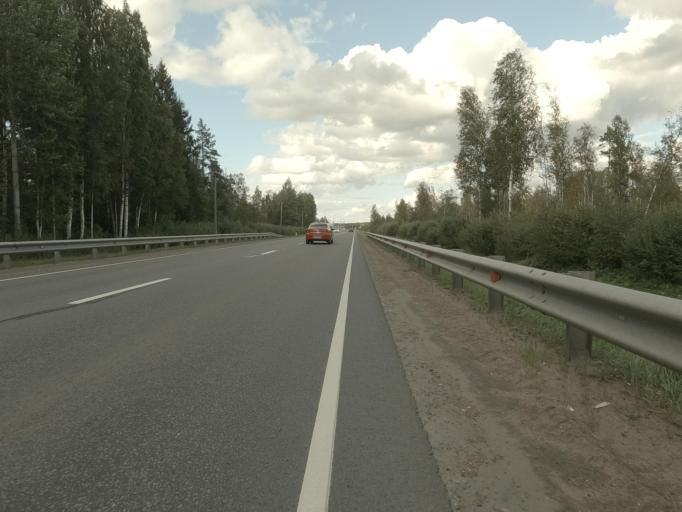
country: RU
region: Leningrad
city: Mga
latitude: 59.7421
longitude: 31.0796
